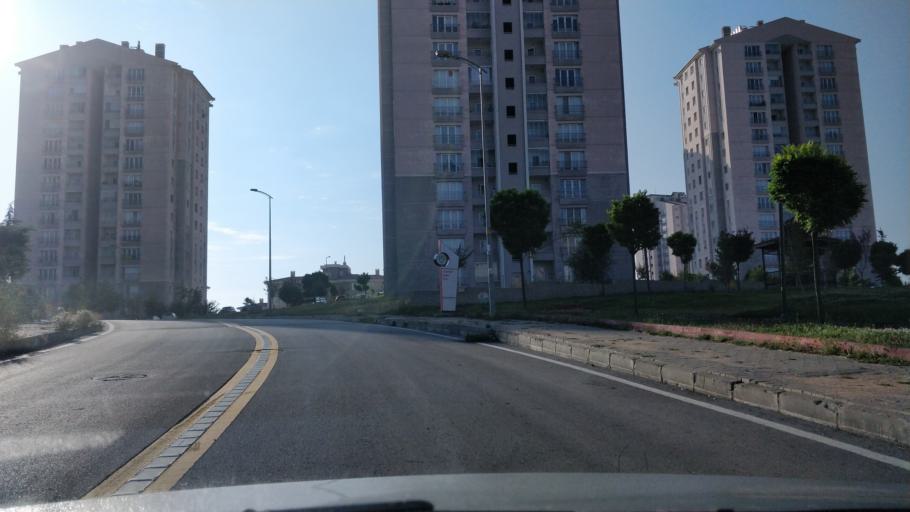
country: TR
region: Ankara
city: Etimesgut
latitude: 39.8428
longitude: 32.5415
